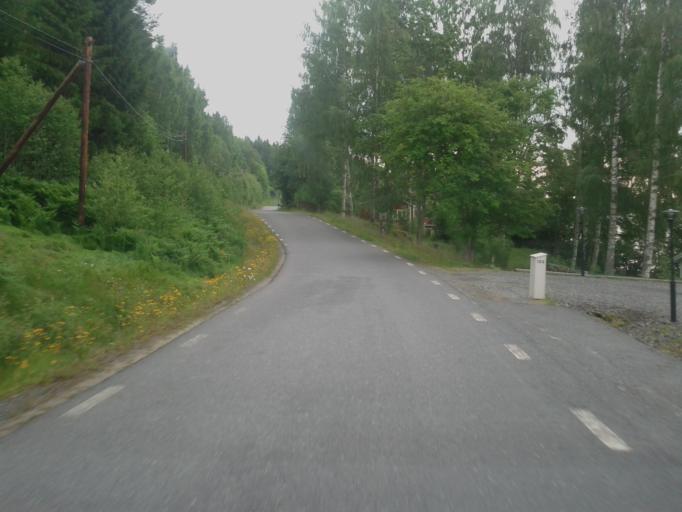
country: SE
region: Vaesternorrland
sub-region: Kramfors Kommun
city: Nordingra
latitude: 63.0623
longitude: 18.3870
